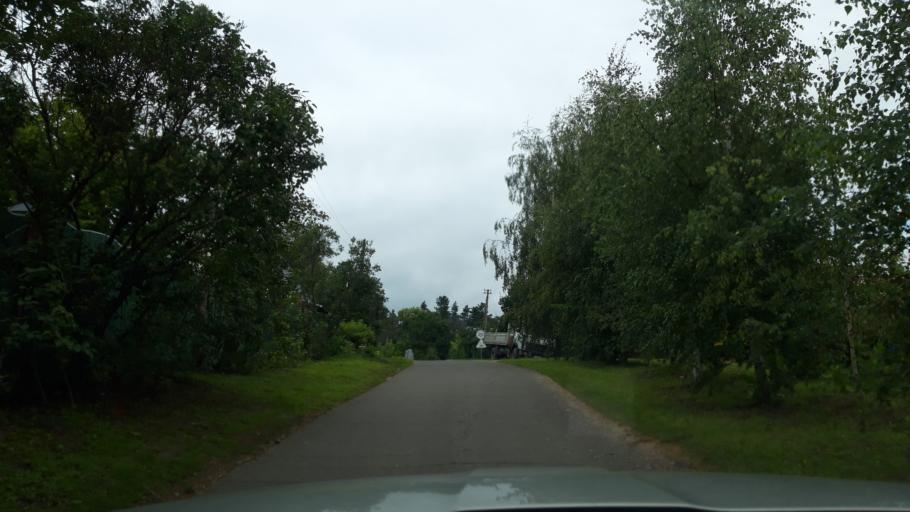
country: RU
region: Moskovskaya
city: Povarovo
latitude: 56.0593
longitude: 37.0592
